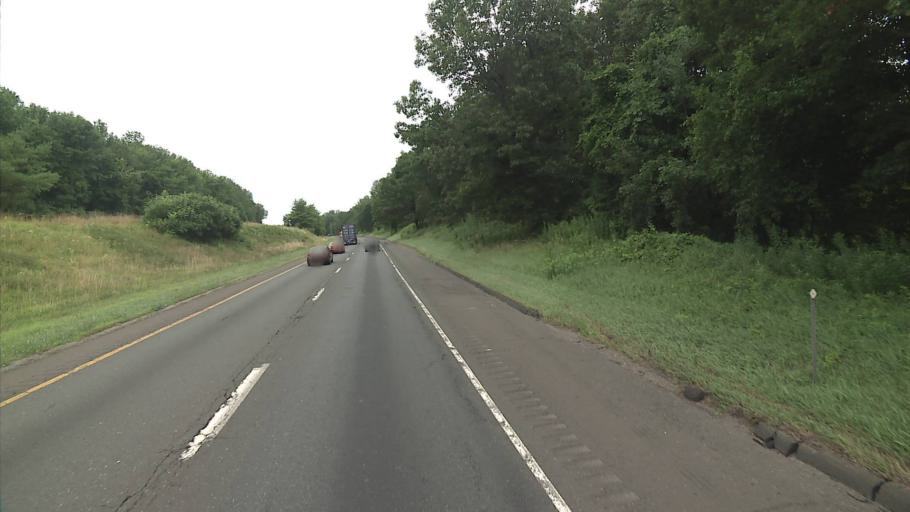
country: US
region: Connecticut
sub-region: Fairfield County
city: Newtown
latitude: 41.4270
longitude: -73.3310
